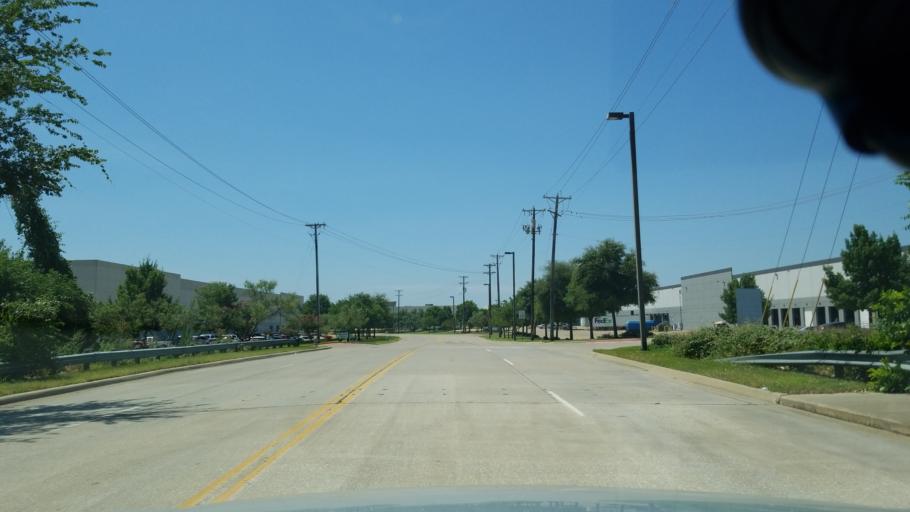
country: US
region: Texas
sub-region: Tarrant County
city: Euless
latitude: 32.8328
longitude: -97.0302
